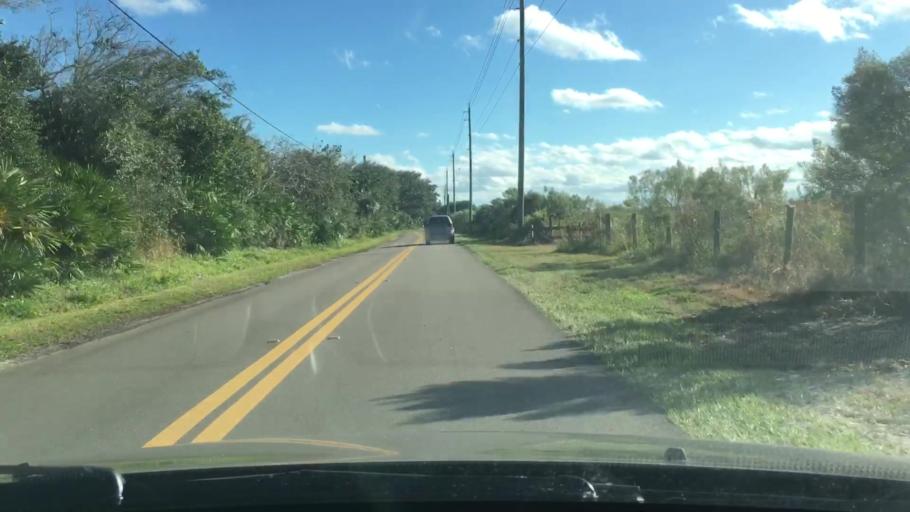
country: US
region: Florida
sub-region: Volusia County
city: Ormond-by-the-Sea
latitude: 29.4059
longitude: -81.0966
